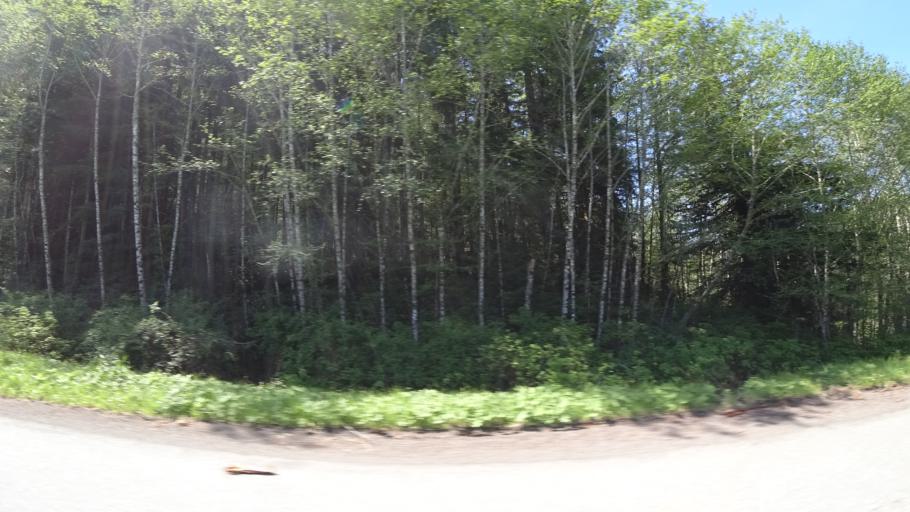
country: US
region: California
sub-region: Humboldt County
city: Westhaven-Moonstone
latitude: 41.4065
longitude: -124.0010
